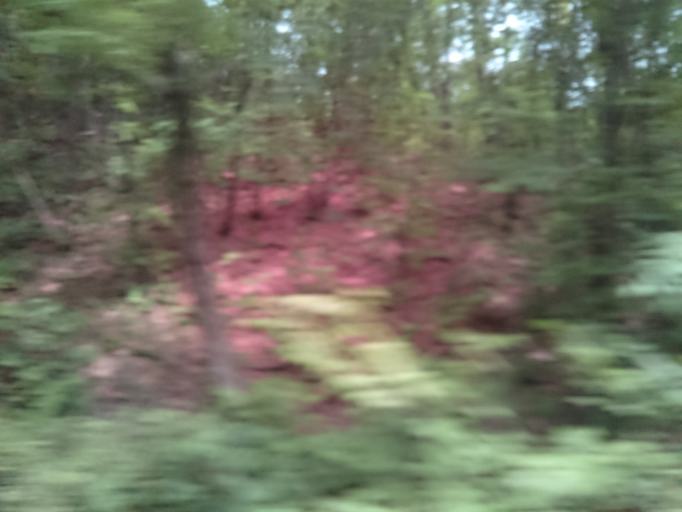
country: KR
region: Jeollabuk-do
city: Wanju
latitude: 35.9005
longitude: 127.1970
